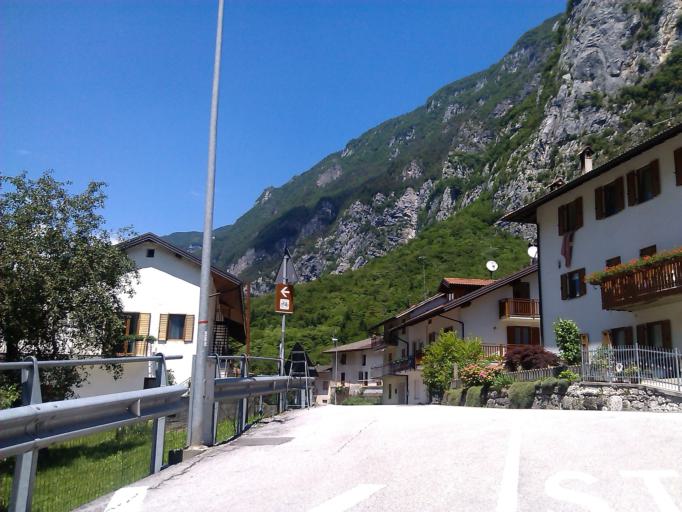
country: IT
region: Veneto
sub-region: Provincia di Vicenza
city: Enego
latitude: 45.9767
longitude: 11.6814
